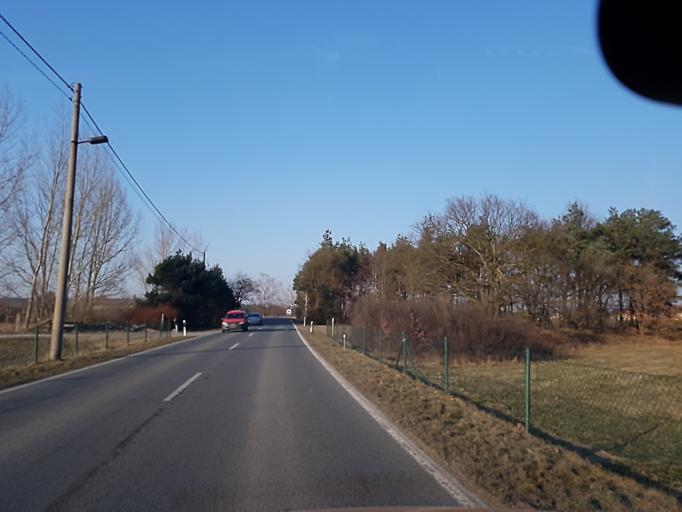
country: DE
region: Brandenburg
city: Ruckersdorf
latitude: 51.6007
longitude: 13.5515
